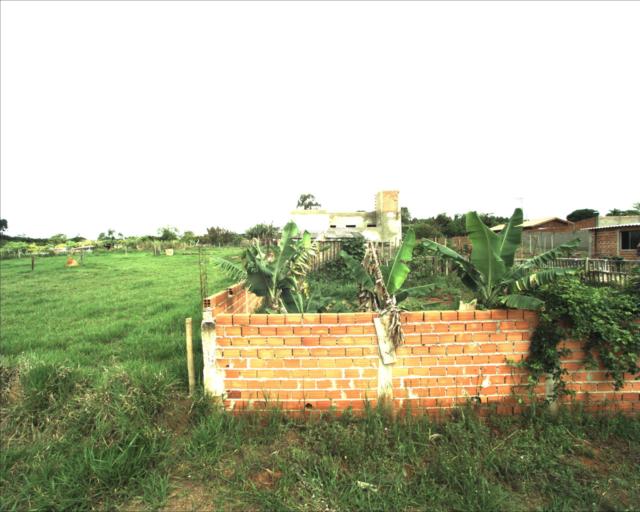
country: BR
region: Sao Paulo
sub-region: Aracoiaba Da Serra
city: Aracoiaba da Serra
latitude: -23.5482
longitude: -47.5473
